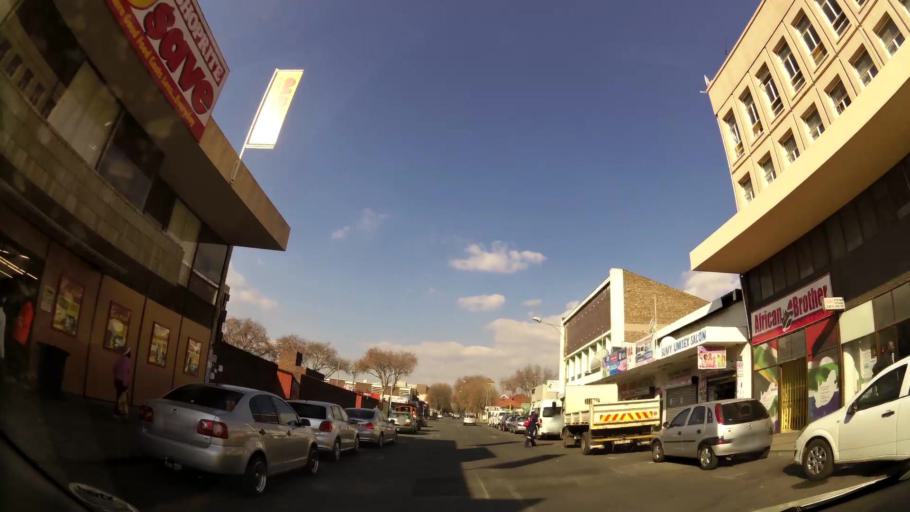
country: ZA
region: Gauteng
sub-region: West Rand District Municipality
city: Krugersdorp
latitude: -26.1041
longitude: 27.7719
